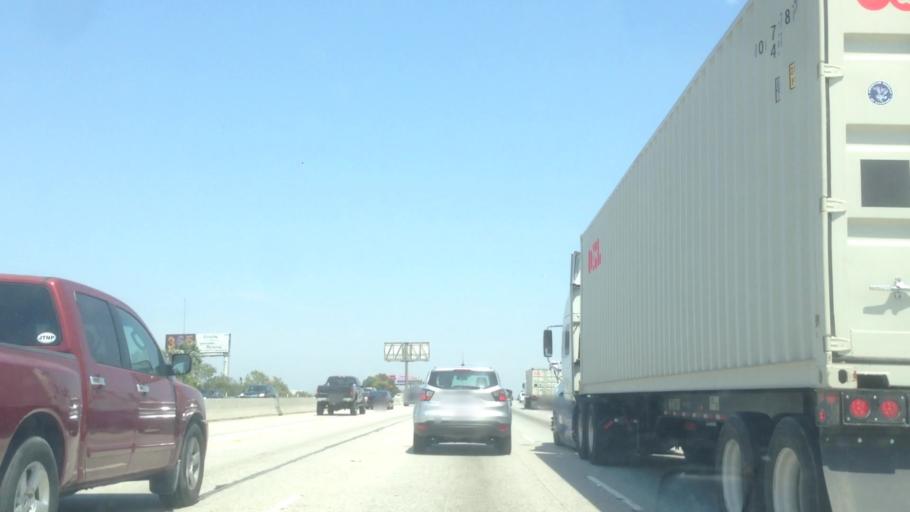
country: US
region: California
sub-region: Los Angeles County
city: Carson
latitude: 33.8255
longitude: -118.2339
